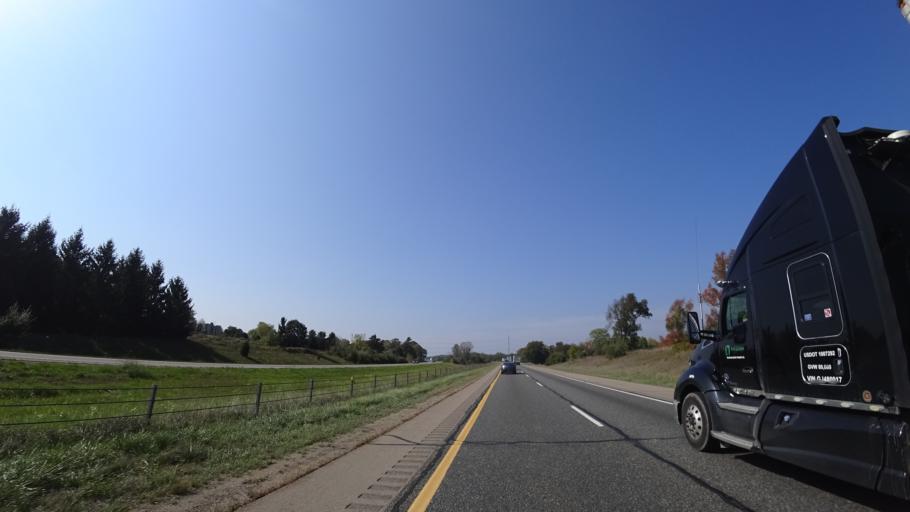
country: US
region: Michigan
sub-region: Washtenaw County
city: Dexter
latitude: 42.2991
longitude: -83.9431
